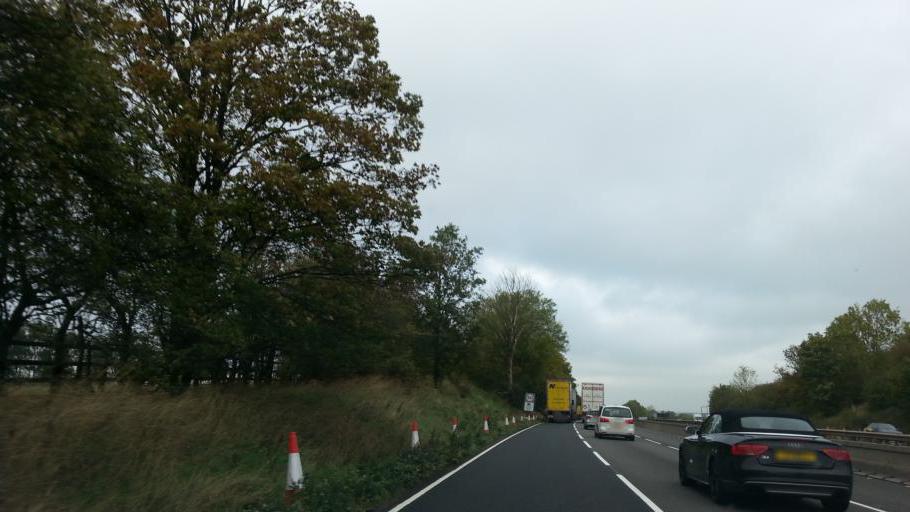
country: GB
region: England
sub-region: Staffordshire
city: Stafford
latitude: 52.8412
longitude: -2.1552
